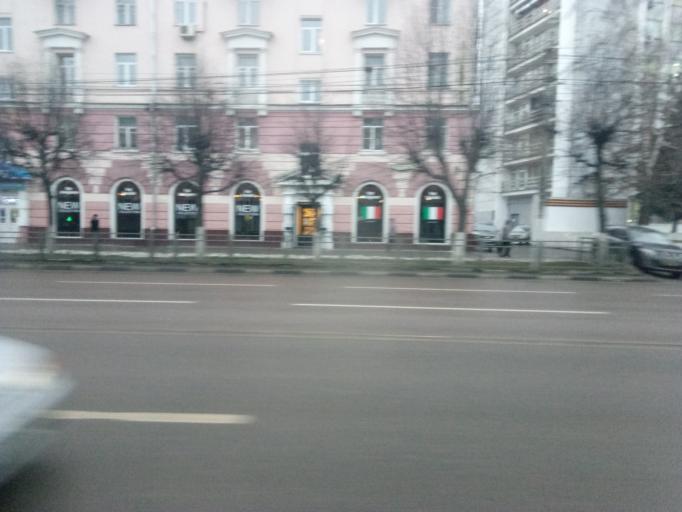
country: RU
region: Tula
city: Tula
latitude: 54.1982
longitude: 37.5893
